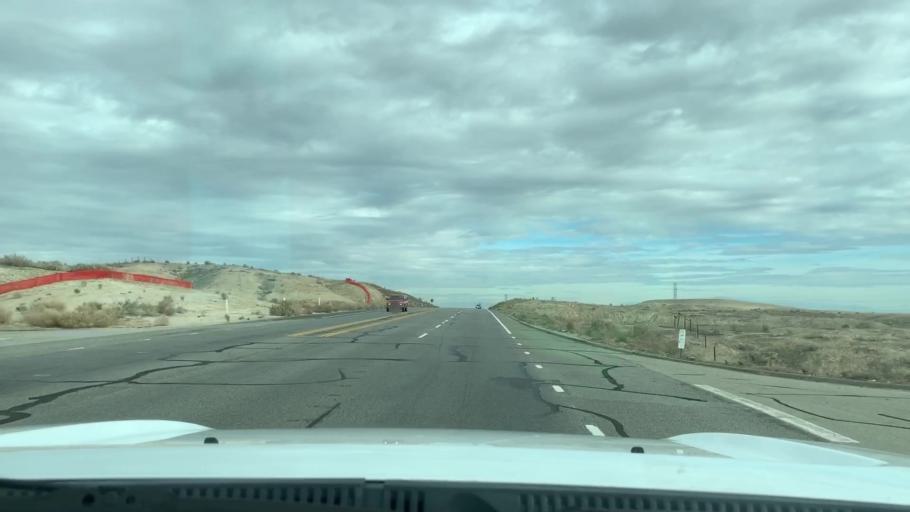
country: US
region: California
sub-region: Kern County
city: Ford City
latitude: 35.2547
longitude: -119.3317
